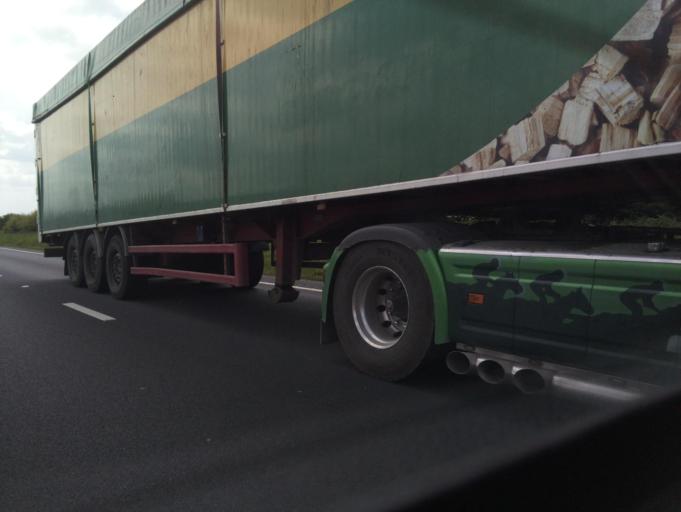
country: GB
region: England
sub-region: Stockton-on-Tees
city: Yarm
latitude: 54.4139
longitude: -1.3198
